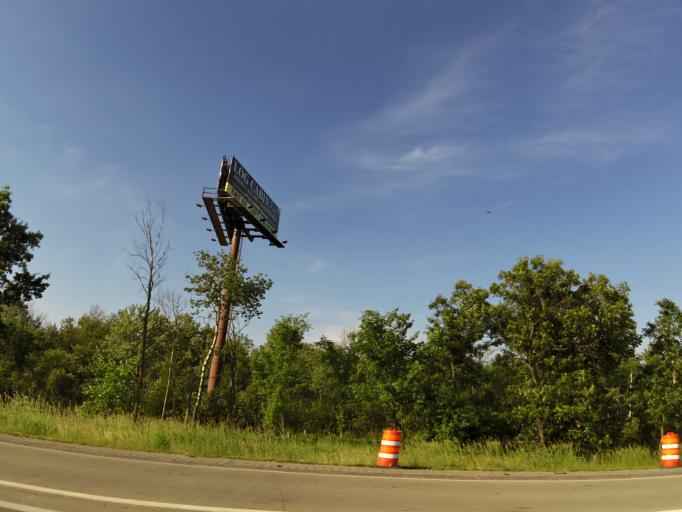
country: US
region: Wisconsin
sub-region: Columbia County
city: Wisconsin Dells
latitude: 43.7203
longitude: -89.8981
